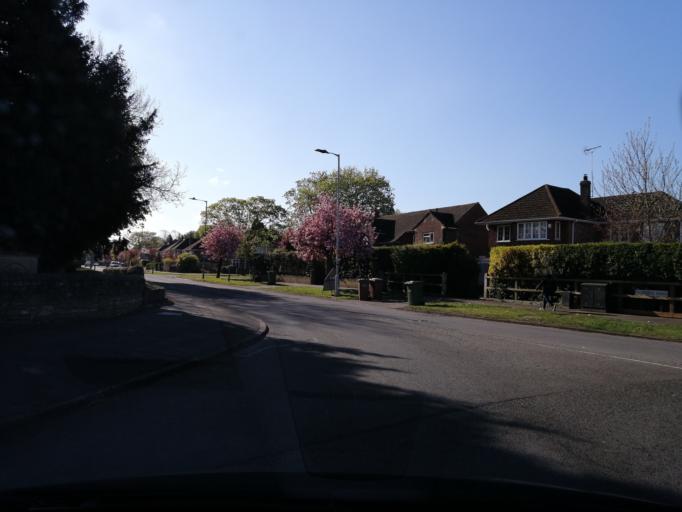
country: GB
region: England
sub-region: Peterborough
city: Peterborough
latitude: 52.6052
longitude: -0.2588
